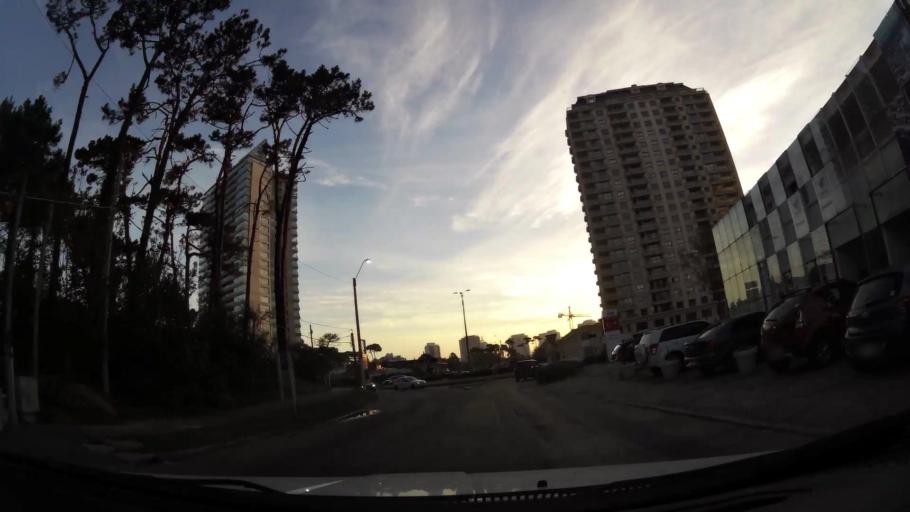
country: UY
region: Maldonado
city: Punta del Este
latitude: -34.9417
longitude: -54.9308
